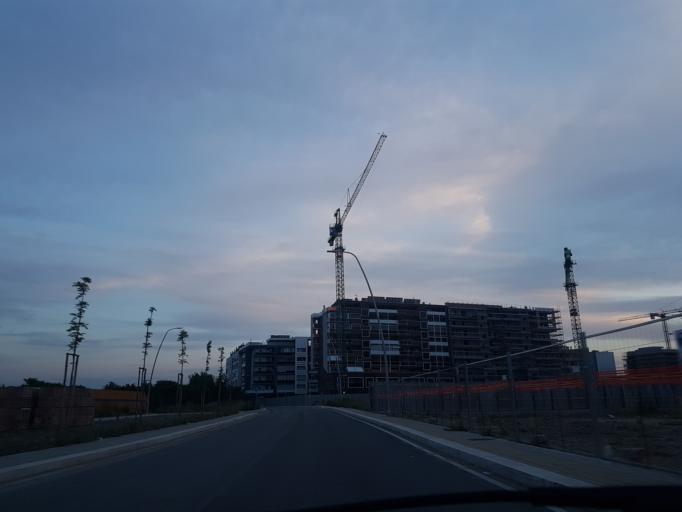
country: IT
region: Apulia
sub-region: Provincia di Barletta - Andria - Trani
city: Barletta
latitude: 41.3054
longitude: 16.2770
